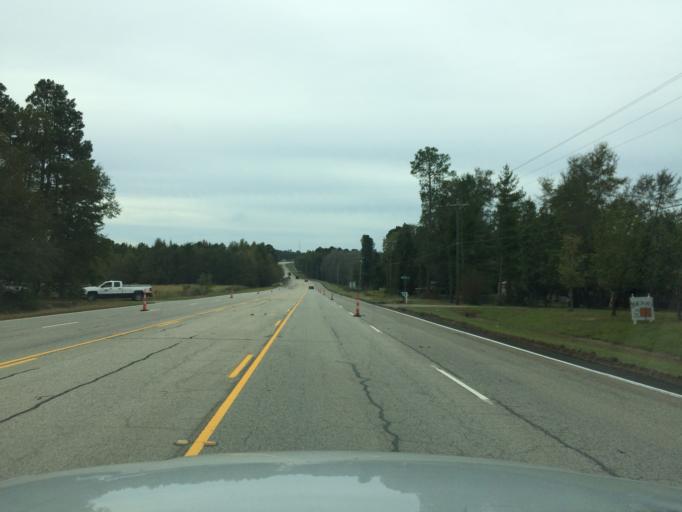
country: US
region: South Carolina
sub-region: Aiken County
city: Aiken
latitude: 33.6099
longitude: -81.6831
